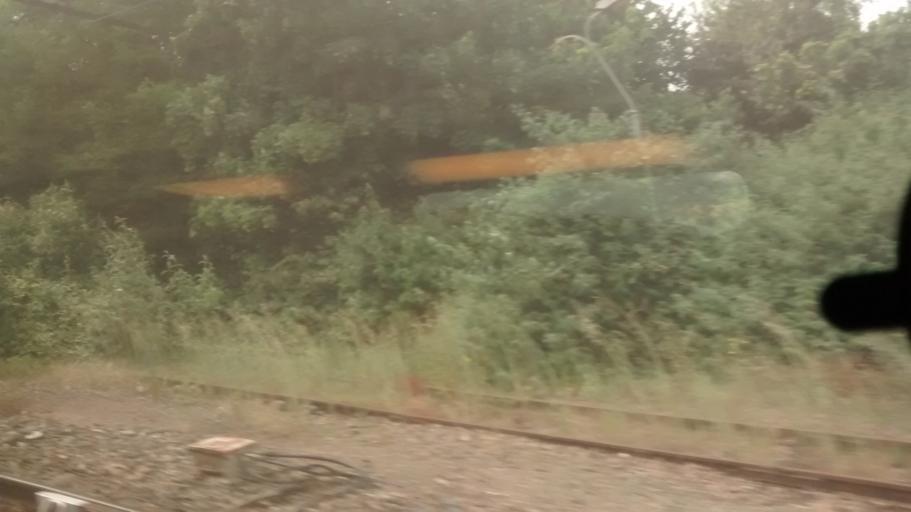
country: FR
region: Ile-de-France
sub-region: Departement de l'Essonne
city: Wissous
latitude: 48.7430
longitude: 2.3259
